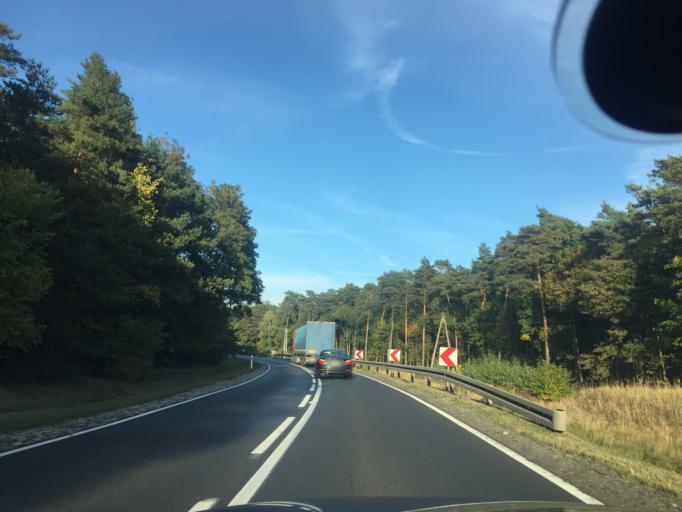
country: PL
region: Kujawsko-Pomorskie
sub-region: Powiat torunski
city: Wielka Nieszawka
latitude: 52.9177
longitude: 18.4957
